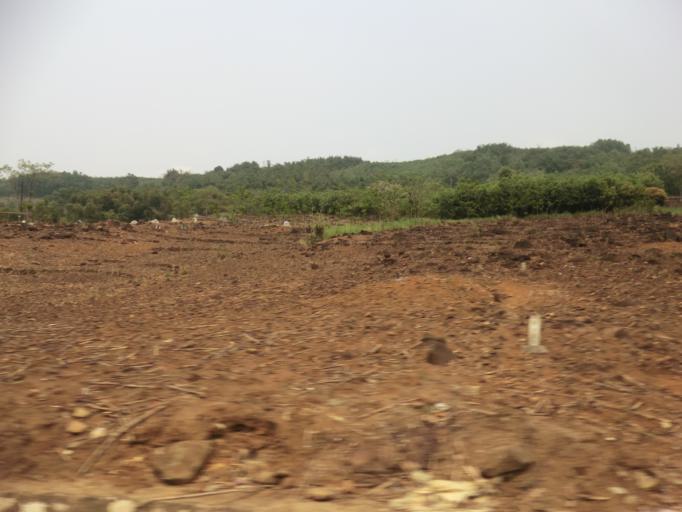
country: VN
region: Thanh Hoa
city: Thi Tran Cam Thuy
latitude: 20.1578
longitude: 105.4648
